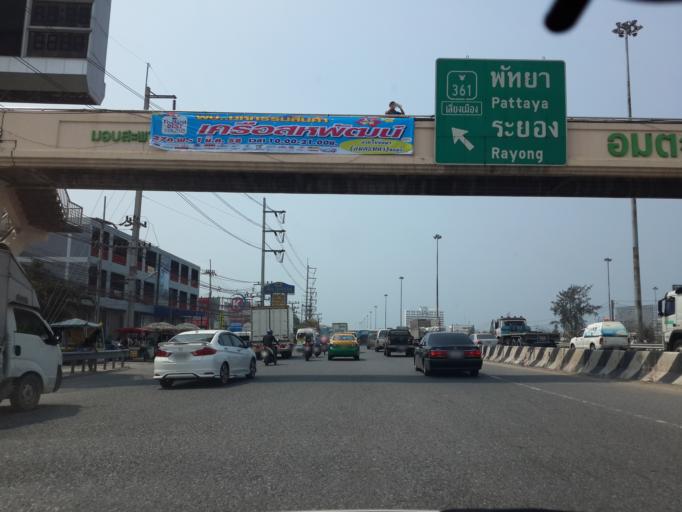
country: TH
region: Chon Buri
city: Chon Buri
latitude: 13.4238
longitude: 101.0001
